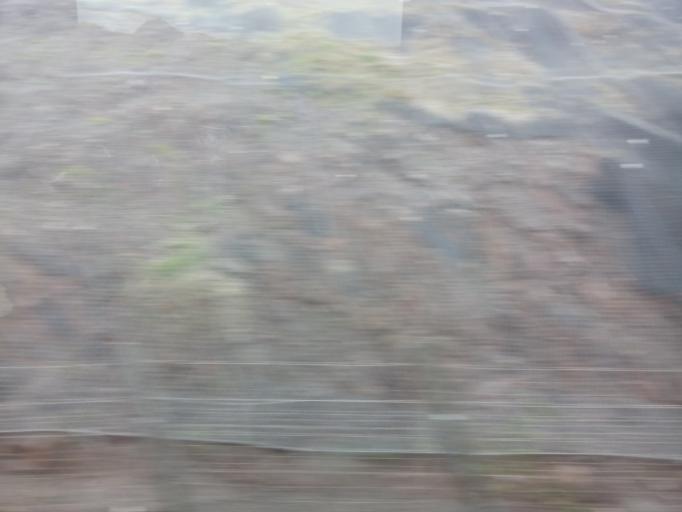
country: GB
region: Scotland
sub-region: The Scottish Borders
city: Eyemouth
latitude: 55.8290
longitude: -2.0563
